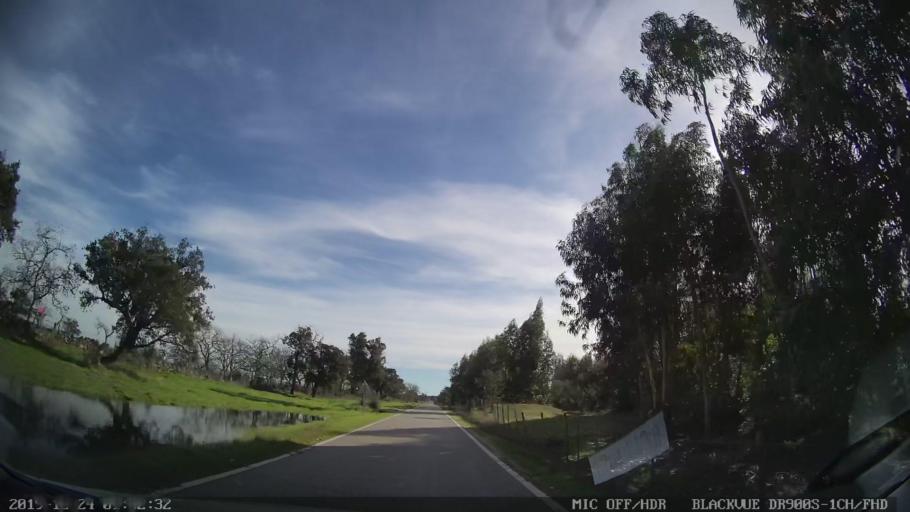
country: PT
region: Portalegre
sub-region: Nisa
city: Nisa
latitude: 39.4923
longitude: -7.7443
